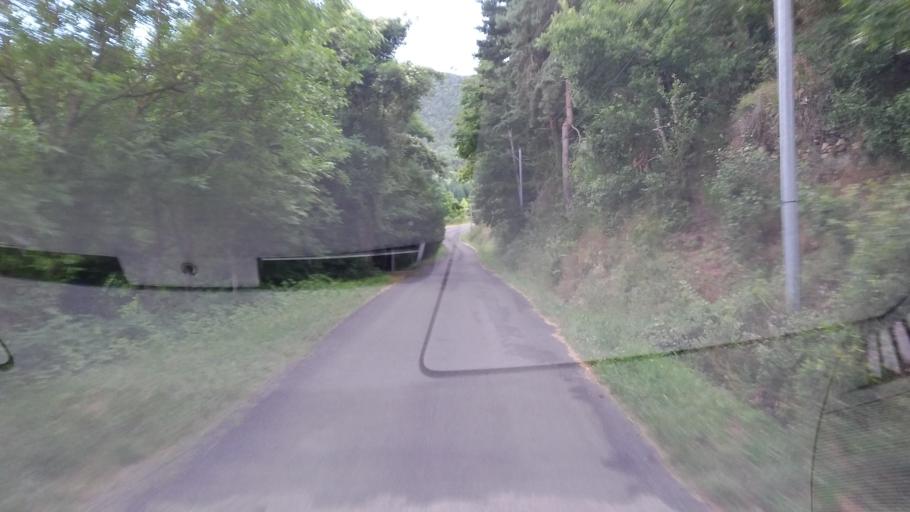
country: FR
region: Languedoc-Roussillon
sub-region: Departement de la Lozere
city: Meyrueis
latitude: 44.0224
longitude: 3.3443
